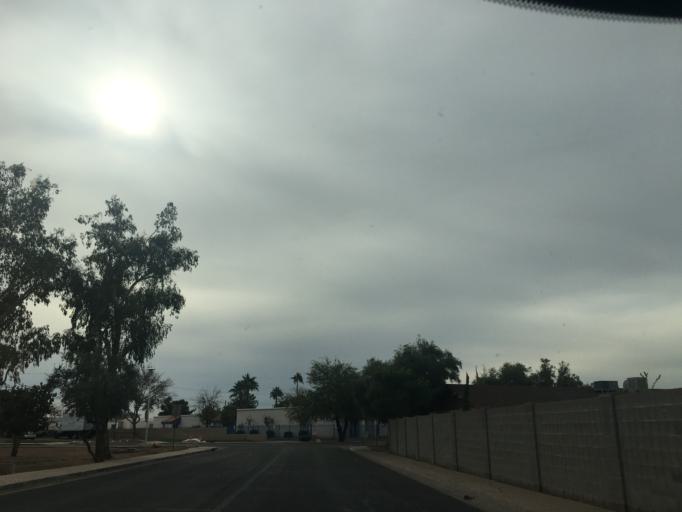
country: US
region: Arizona
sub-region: Maricopa County
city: Gilbert
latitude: 33.3608
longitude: -111.7961
